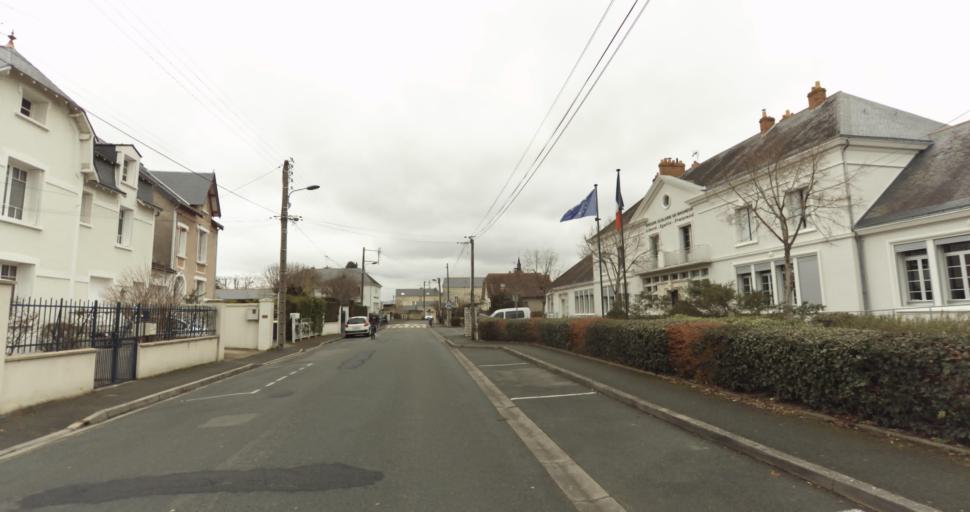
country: FR
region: Pays de la Loire
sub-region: Departement de Maine-et-Loire
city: Saumur
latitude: 47.2440
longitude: -0.0942
